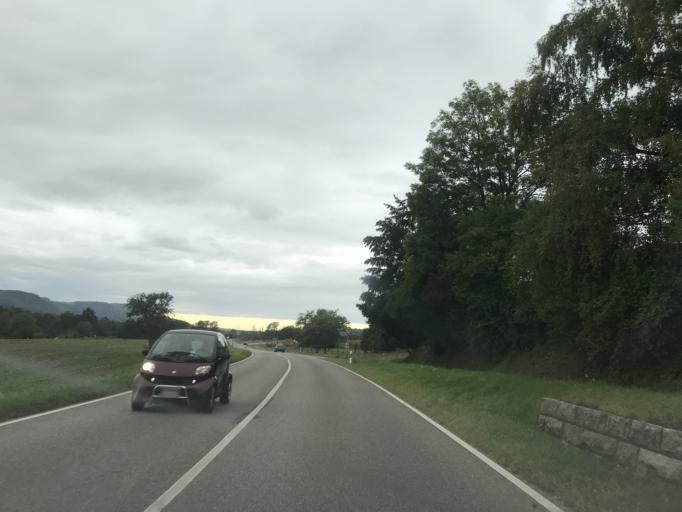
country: DE
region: Baden-Wuerttemberg
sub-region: Freiburg Region
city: Murg
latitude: 47.5586
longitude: 7.9982
